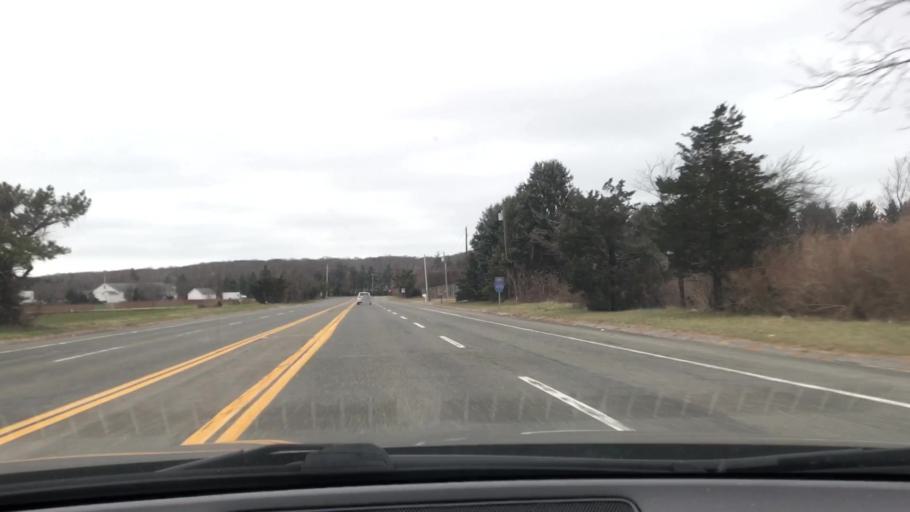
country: US
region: New York
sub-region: Suffolk County
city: Aquebogue
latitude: 40.9643
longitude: -72.6551
